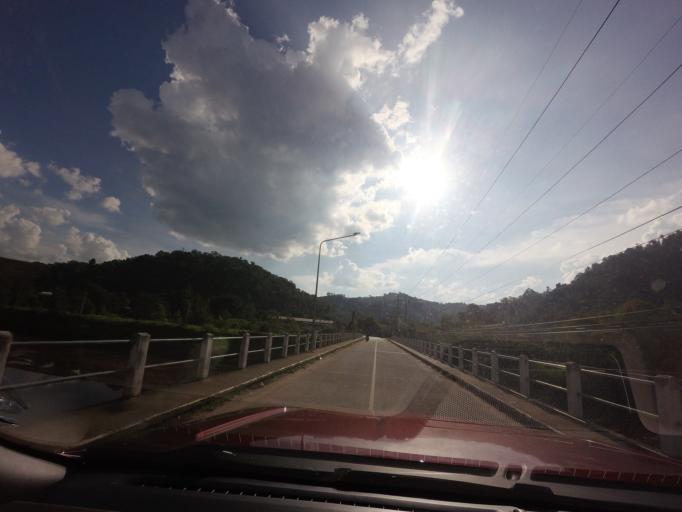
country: TH
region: Yala
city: Than To
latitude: 6.1605
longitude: 101.2762
